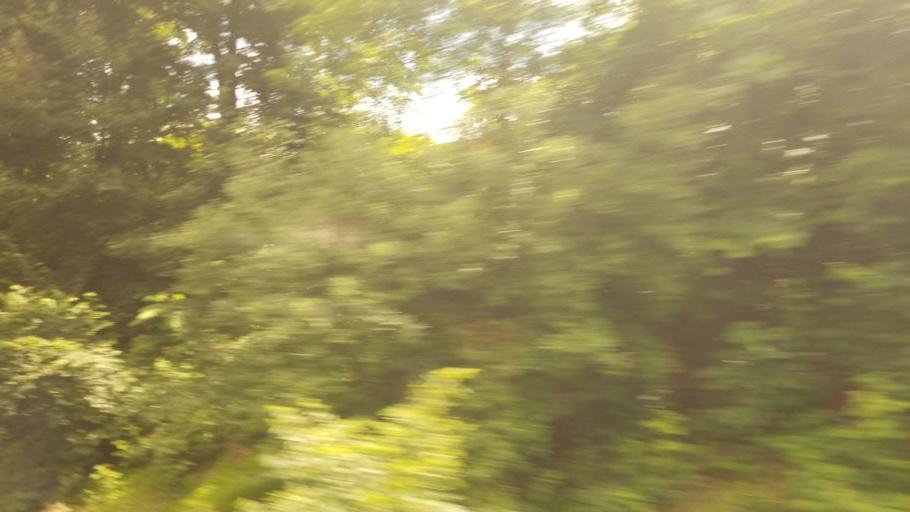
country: US
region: Maryland
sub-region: Montgomery County
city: Gaithersburg
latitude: 39.1516
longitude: -77.2315
